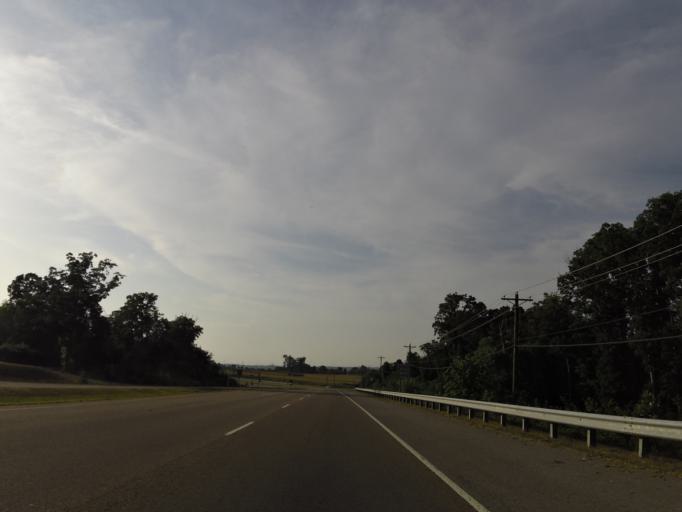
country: US
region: Tennessee
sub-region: Loudon County
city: Lenoir City
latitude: 35.7706
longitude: -84.2311
